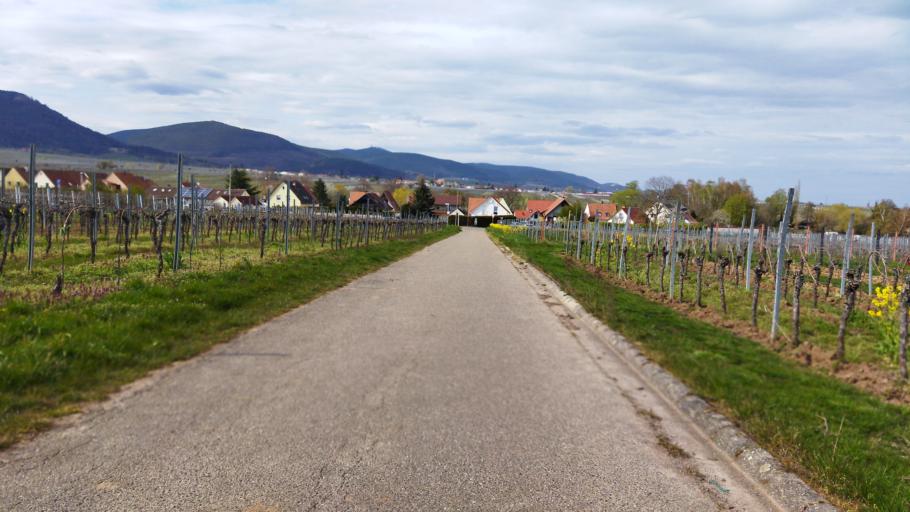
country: DE
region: Rheinland-Pfalz
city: Hainfeld
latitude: 49.2551
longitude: 8.1114
